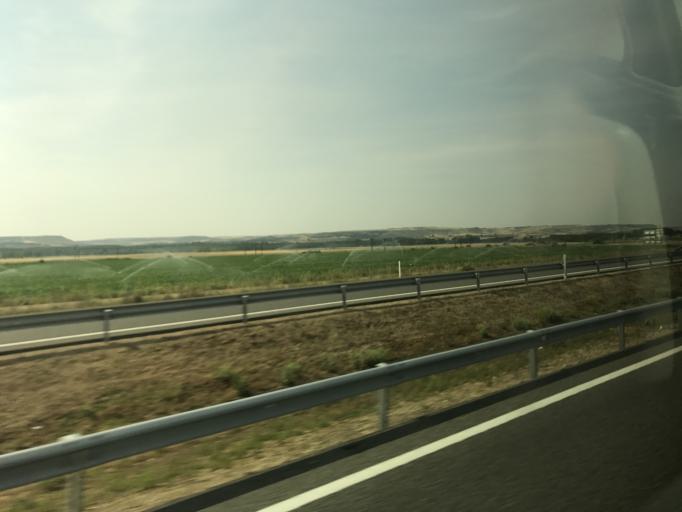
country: ES
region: Castille and Leon
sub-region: Provincia de Burgos
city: Villazopeque
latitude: 42.1921
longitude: -4.0319
